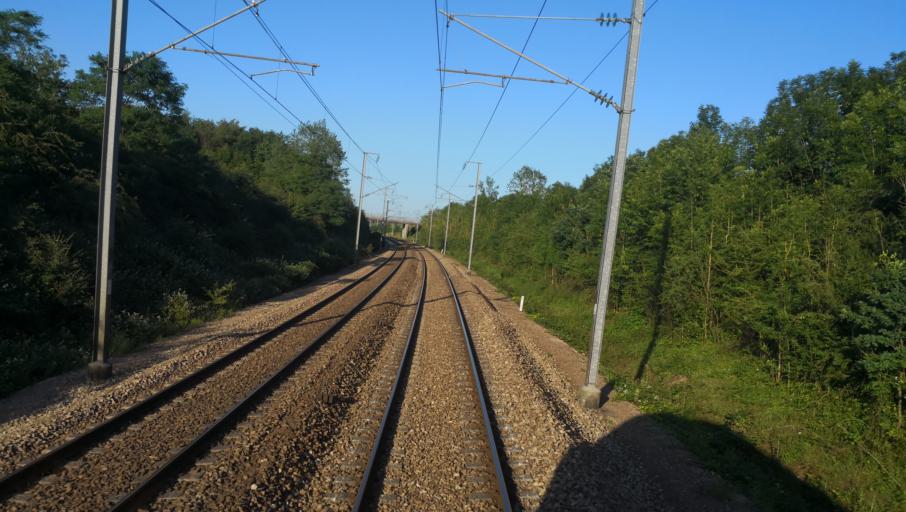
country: FR
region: Lower Normandy
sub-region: Departement du Calvados
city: La Vespiere
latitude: 49.0681
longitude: 0.4337
